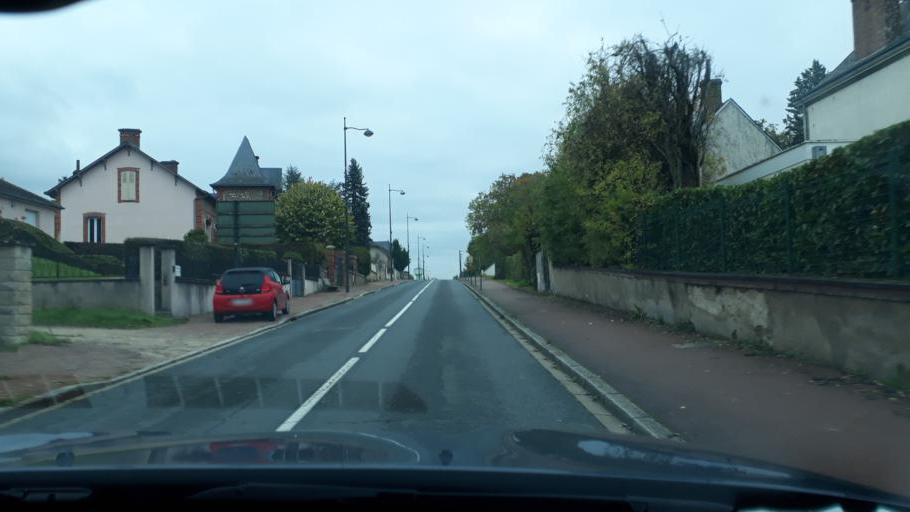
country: FR
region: Centre
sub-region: Departement du Loiret
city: Bray-en-Val
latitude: 47.8143
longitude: 2.4033
